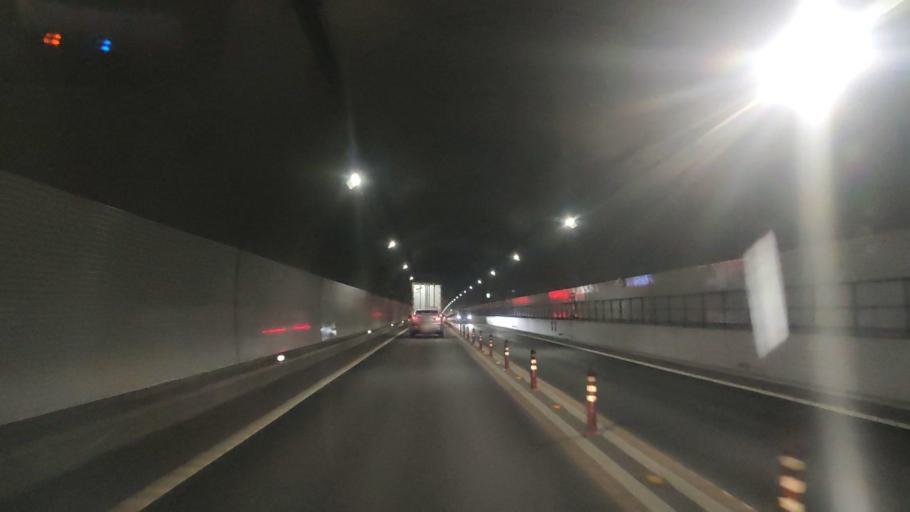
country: JP
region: Fukuoka
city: Kanda
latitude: 33.7620
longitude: 130.9616
